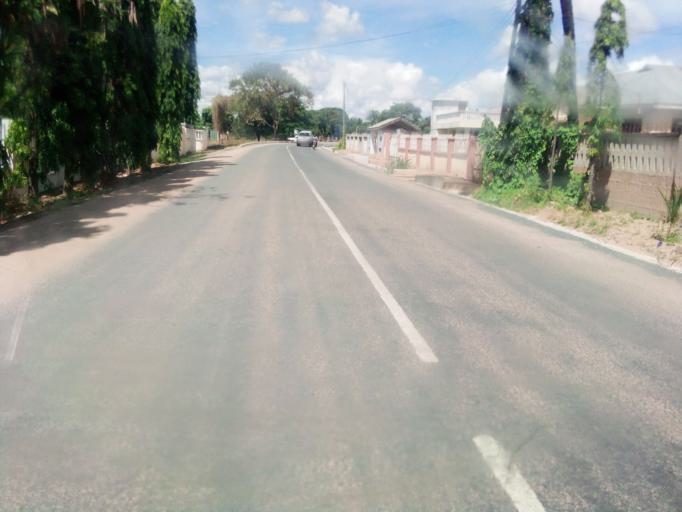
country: TZ
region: Dodoma
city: Kisasa
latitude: -6.1648
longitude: 35.7703
